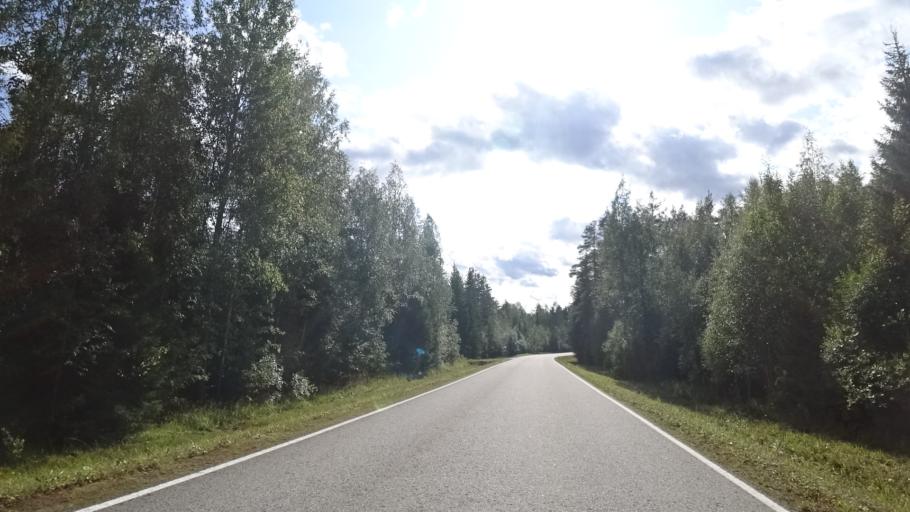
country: RU
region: Republic of Karelia
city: Vyartsilya
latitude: 62.2293
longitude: 30.6721
